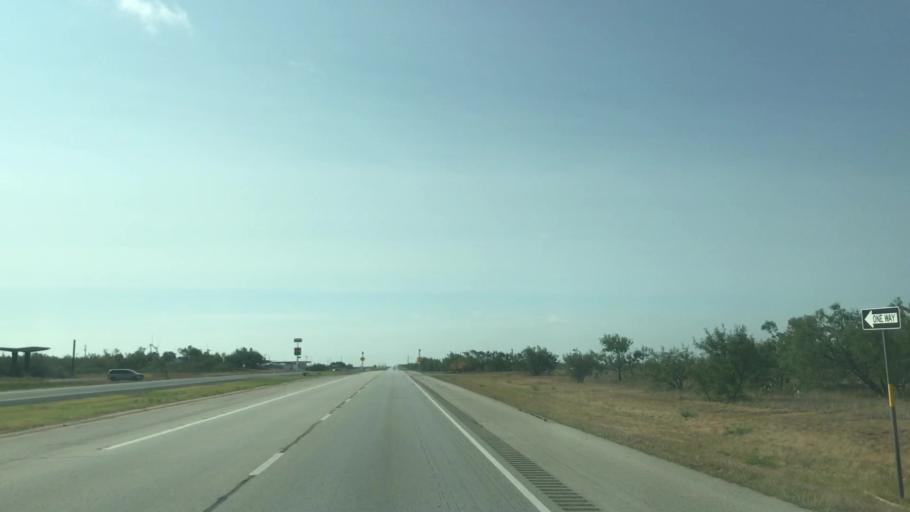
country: US
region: Texas
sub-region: Scurry County
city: Snyder
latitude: 32.6386
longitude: -100.7673
